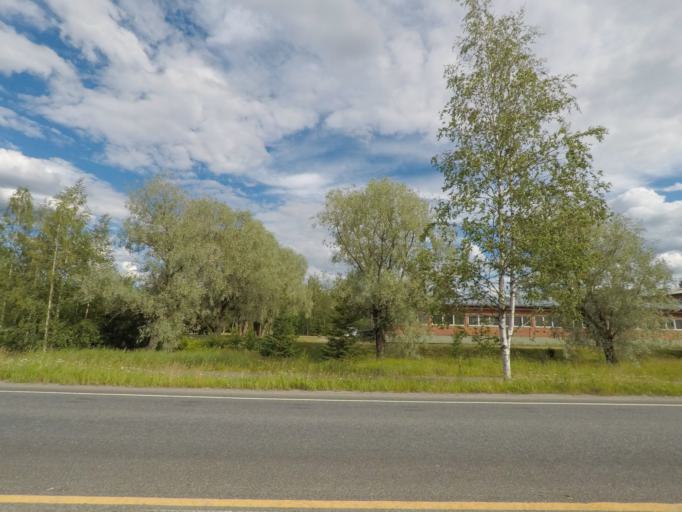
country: FI
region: Paijanne Tavastia
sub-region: Lahti
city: Lahti
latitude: 60.9472
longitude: 25.6070
